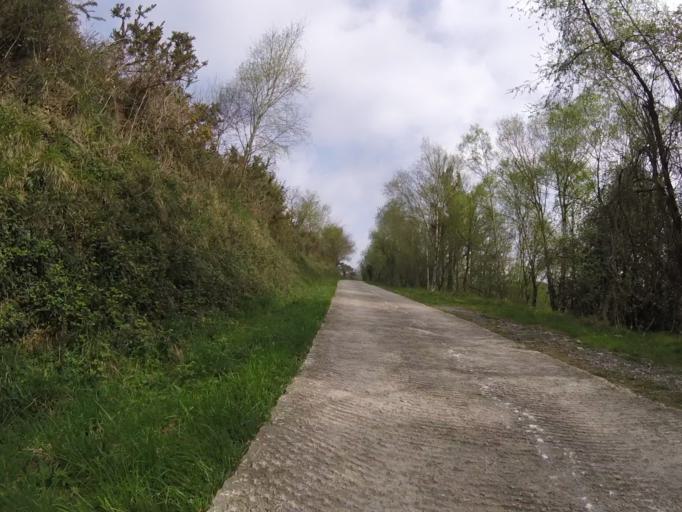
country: ES
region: Basque Country
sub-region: Provincia de Guipuzcoa
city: Asteasu
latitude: 43.2269
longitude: -2.0941
